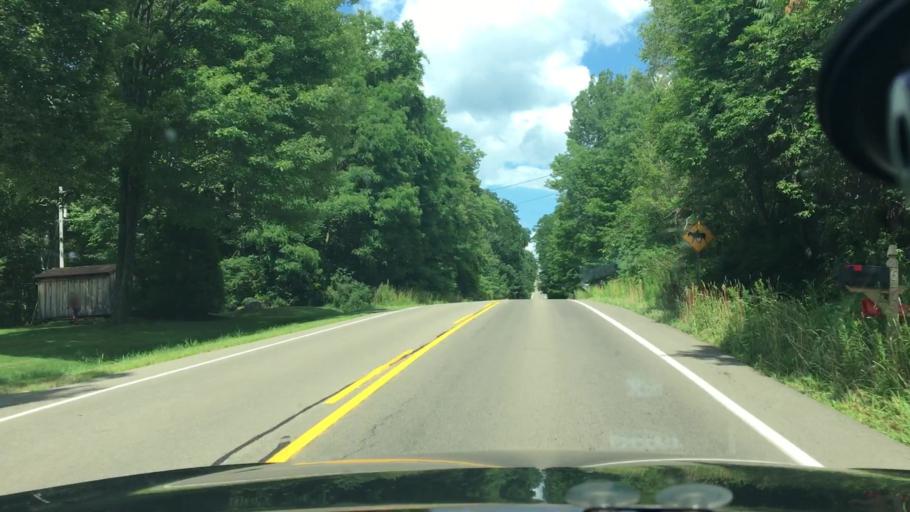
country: US
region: New York
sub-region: Chautauqua County
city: Lakewood
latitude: 42.1770
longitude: -79.3632
